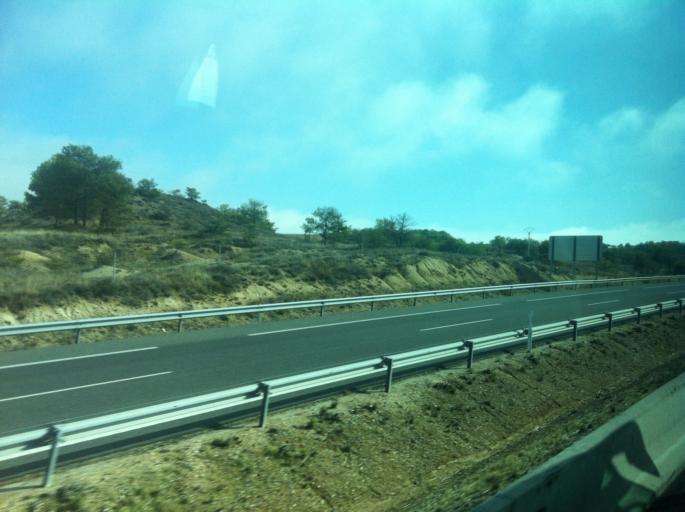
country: ES
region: Castille and Leon
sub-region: Provincia de Burgos
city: Oquillas
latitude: 41.8164
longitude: -3.7024
